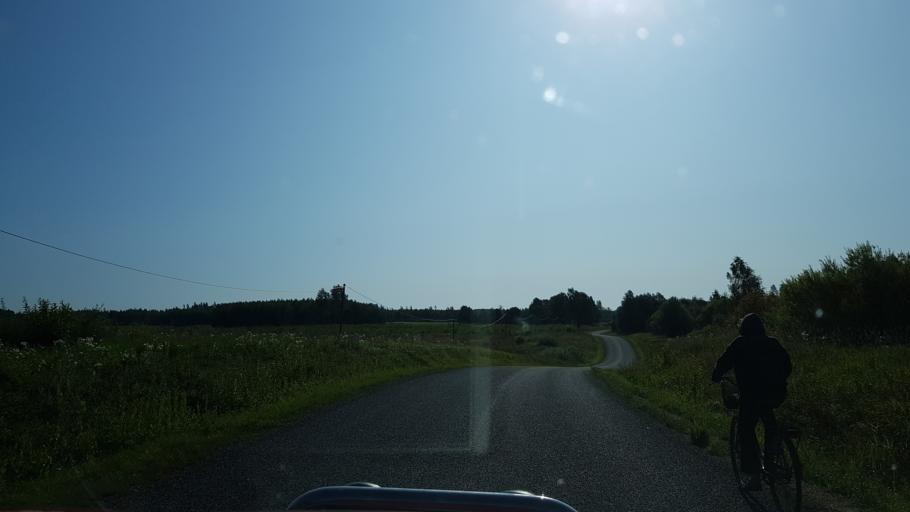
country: LV
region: Apes Novads
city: Ape
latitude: 57.6555
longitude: 26.7355
